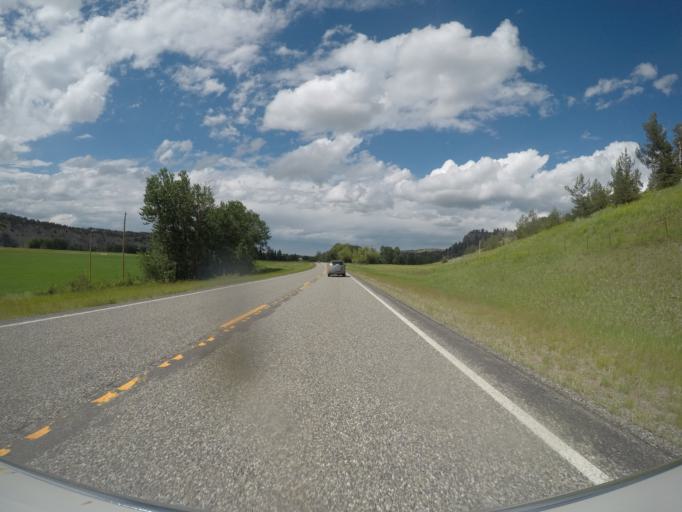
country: US
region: Montana
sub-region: Sweet Grass County
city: Big Timber
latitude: 45.7186
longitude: -109.9976
